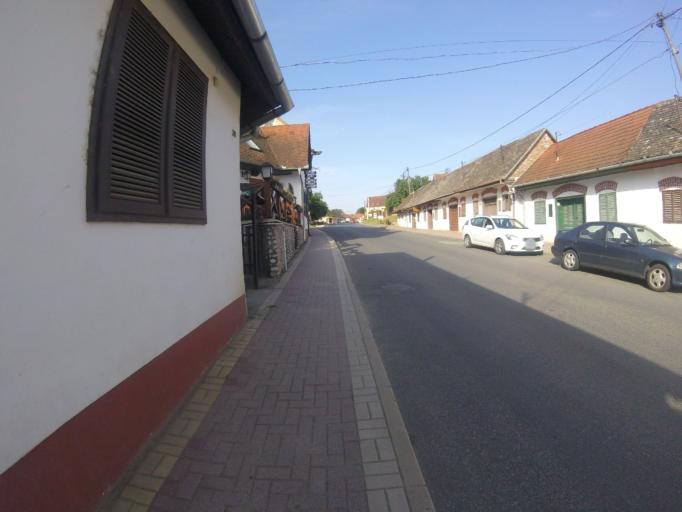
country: HU
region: Baranya
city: Villany
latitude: 45.8674
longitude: 18.4523
